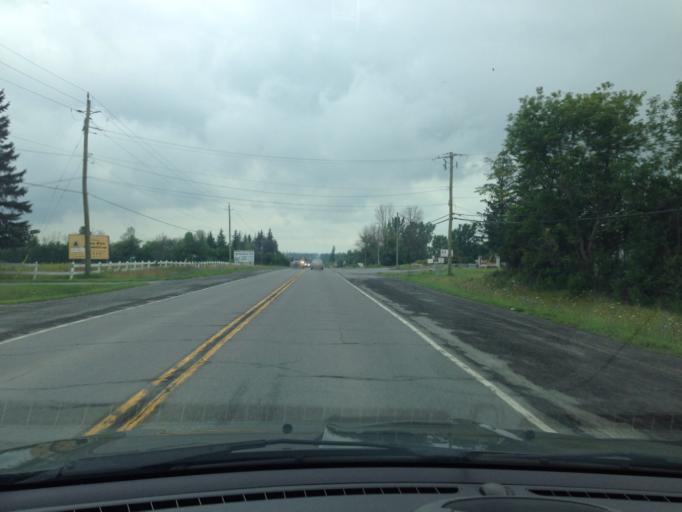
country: CA
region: Ontario
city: Ottawa
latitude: 45.2999
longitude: -75.5817
